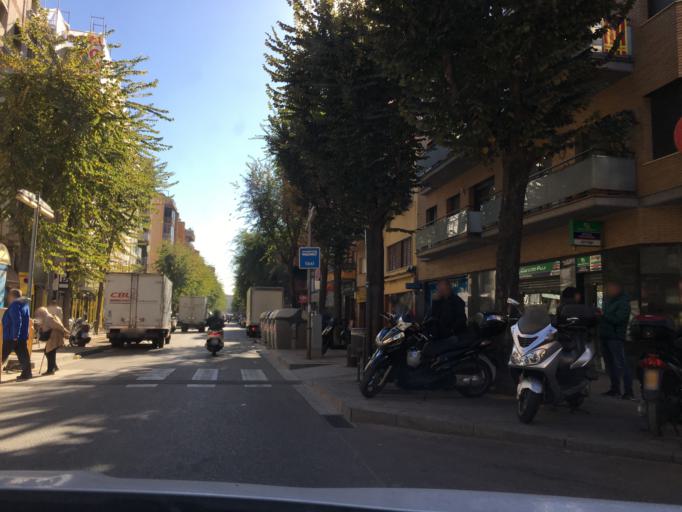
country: ES
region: Catalonia
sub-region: Provincia de Barcelona
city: Santa Coloma de Gramenet
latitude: 41.4501
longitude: 2.2071
